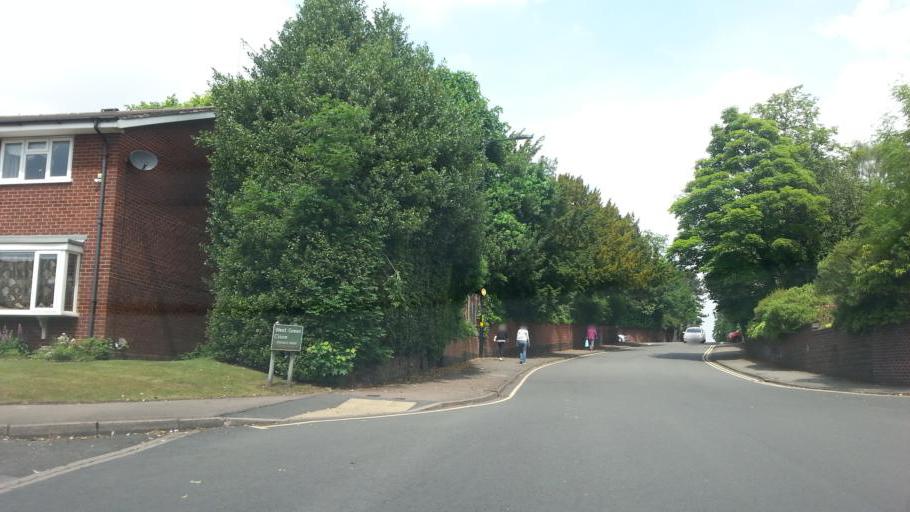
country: GB
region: England
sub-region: City and Borough of Birmingham
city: Birmingham
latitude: 52.4678
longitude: -1.9140
